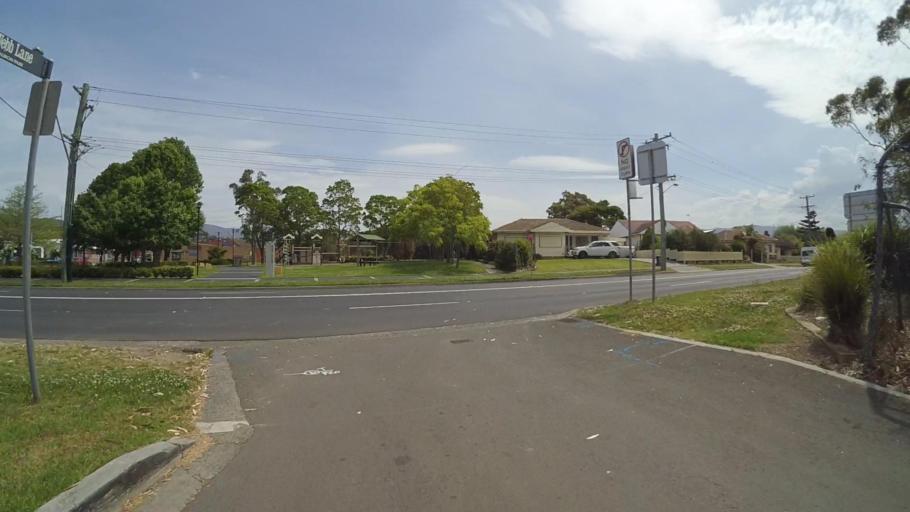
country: AU
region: New South Wales
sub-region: Shellharbour
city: Albion Park Rail
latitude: -34.5701
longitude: 150.7749
